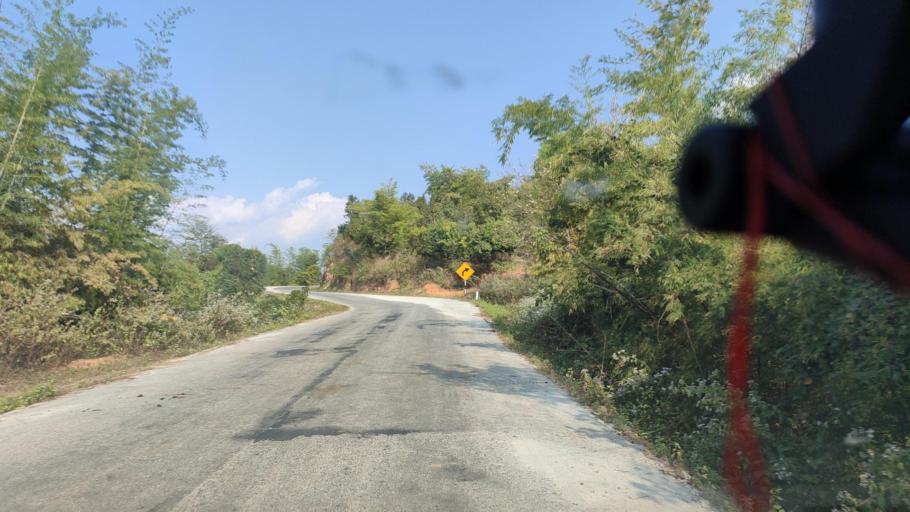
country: CN
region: Yunnan
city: Nayun
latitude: 21.4496
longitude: 99.6518
